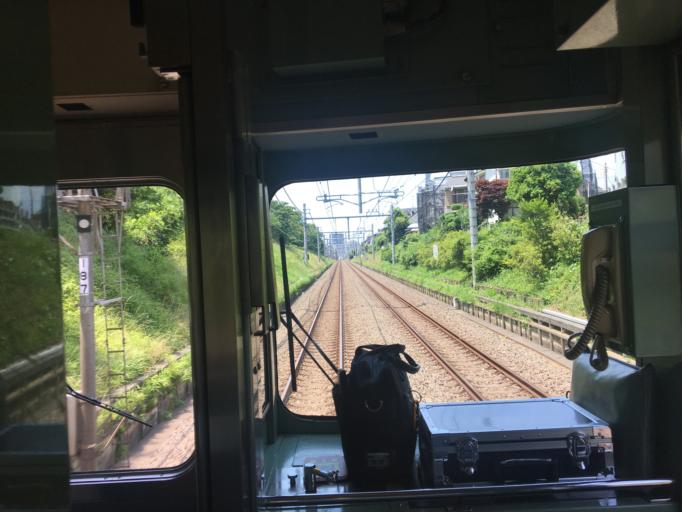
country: JP
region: Tokyo
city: Tanashicho
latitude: 35.7653
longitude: 139.5291
